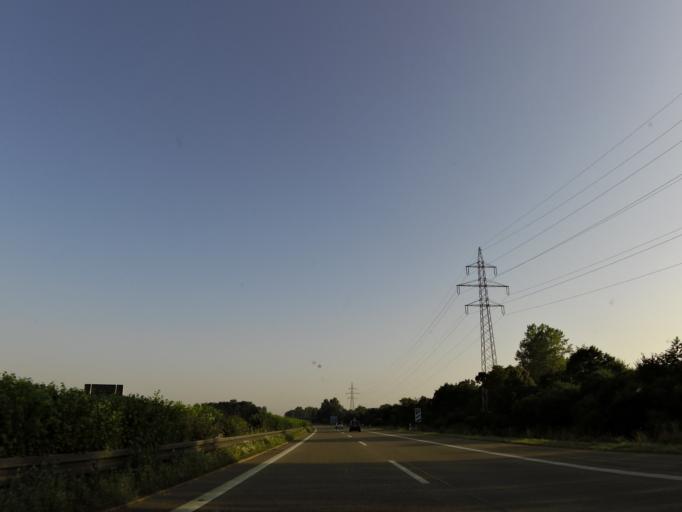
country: DE
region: Baden-Wuerttemberg
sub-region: Tuebingen Region
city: Dettingen an der Iller
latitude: 48.1019
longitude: 10.1311
